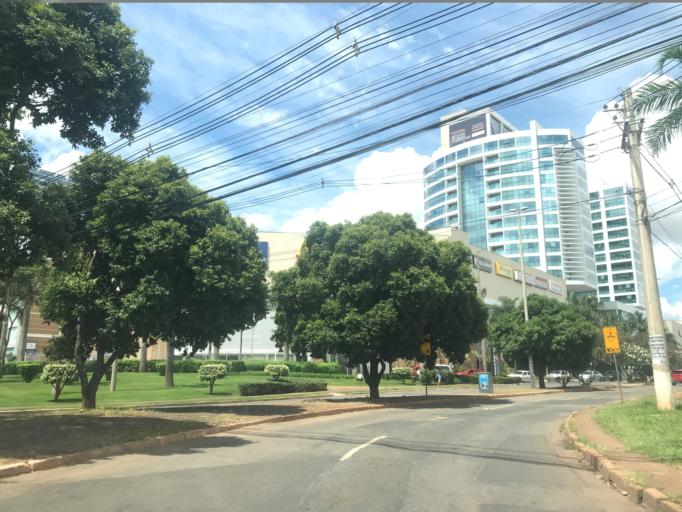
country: BR
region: Federal District
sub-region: Brasilia
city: Brasilia
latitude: -15.8431
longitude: -48.0450
